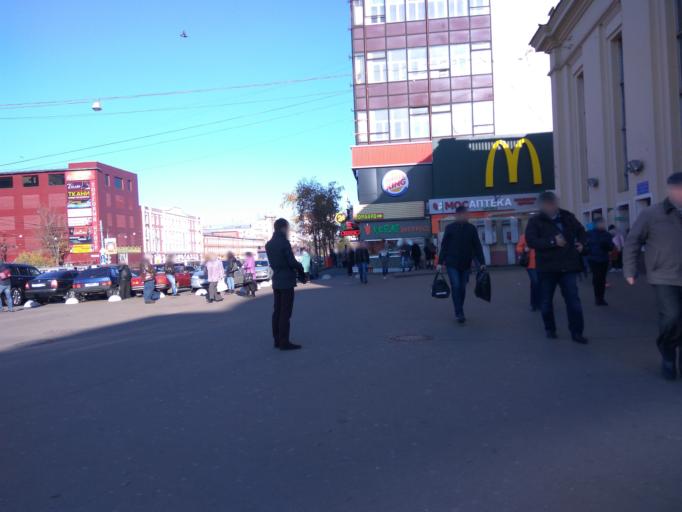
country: RU
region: Moscow
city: Lefortovo
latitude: 55.7830
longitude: 37.7192
